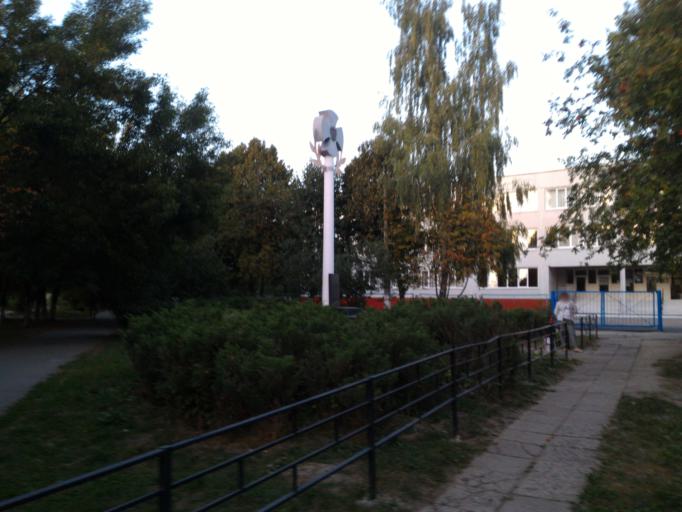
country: RU
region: Kursk
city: Kursk
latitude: 51.7348
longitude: 36.1286
